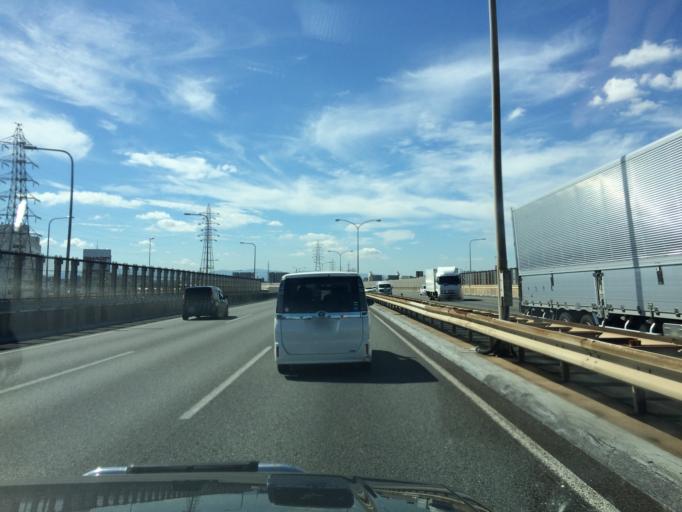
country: JP
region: Osaka
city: Yao
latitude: 34.6249
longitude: 135.5764
